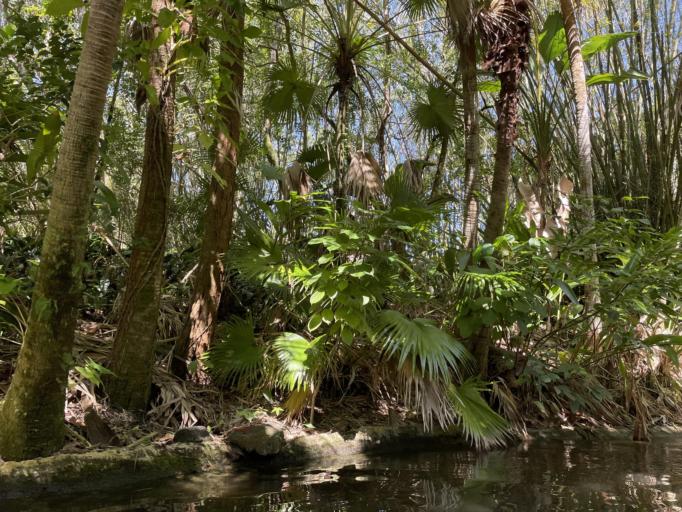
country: US
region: Florida
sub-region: Orange County
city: Bay Hill
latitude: 28.4172
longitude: -81.5831
